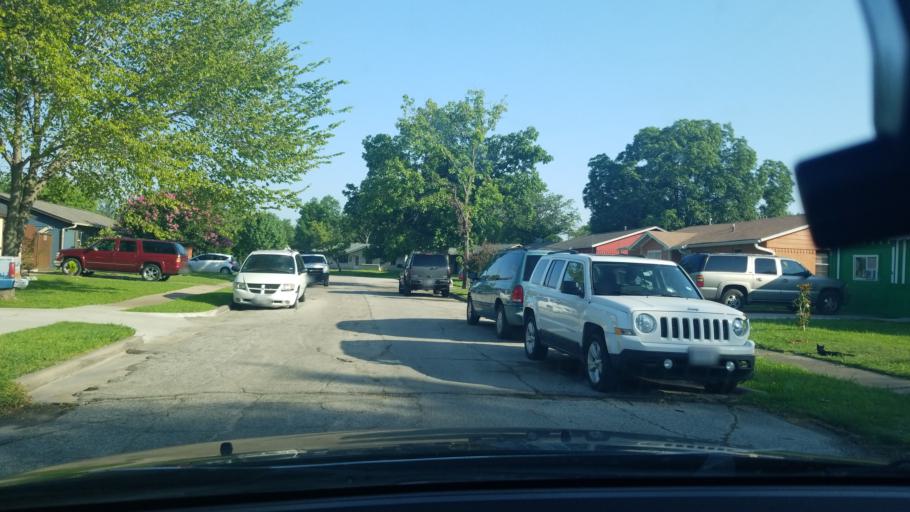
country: US
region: Texas
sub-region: Dallas County
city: Mesquite
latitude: 32.8106
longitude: -96.6375
